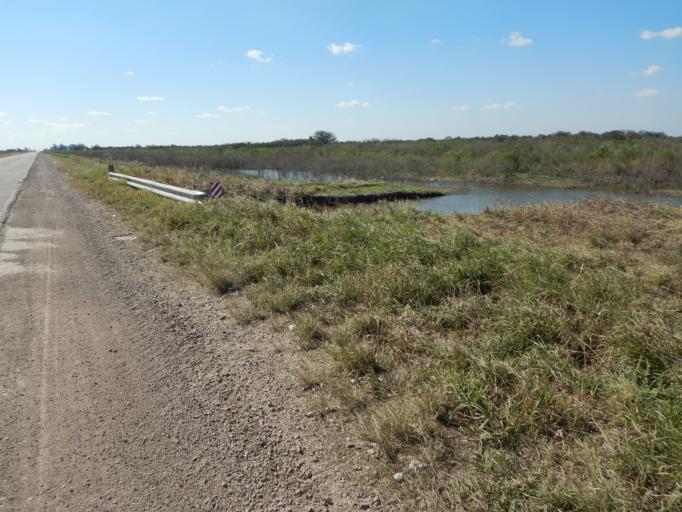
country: AR
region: Santiago del Estero
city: Los Juries
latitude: -28.6232
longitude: -61.5214
